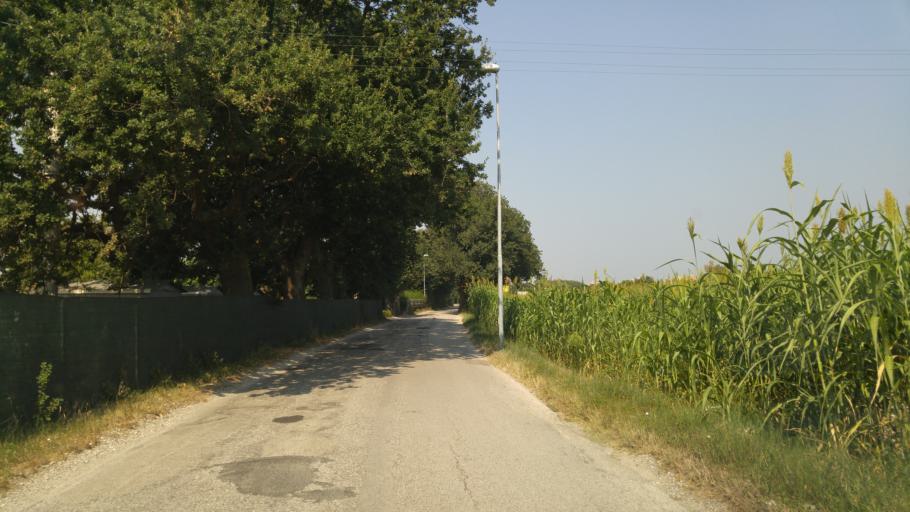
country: IT
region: The Marches
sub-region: Provincia di Pesaro e Urbino
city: Fano
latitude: 43.8316
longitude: 13.0357
